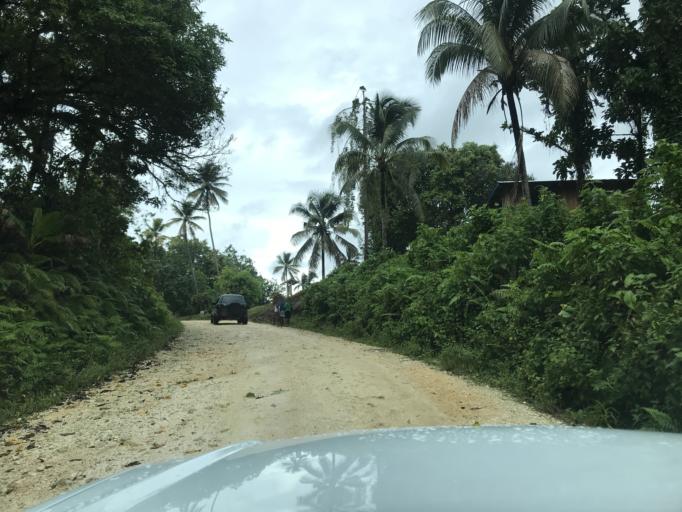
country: SB
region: Malaita
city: Auki
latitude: -8.6882
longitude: 160.6967
